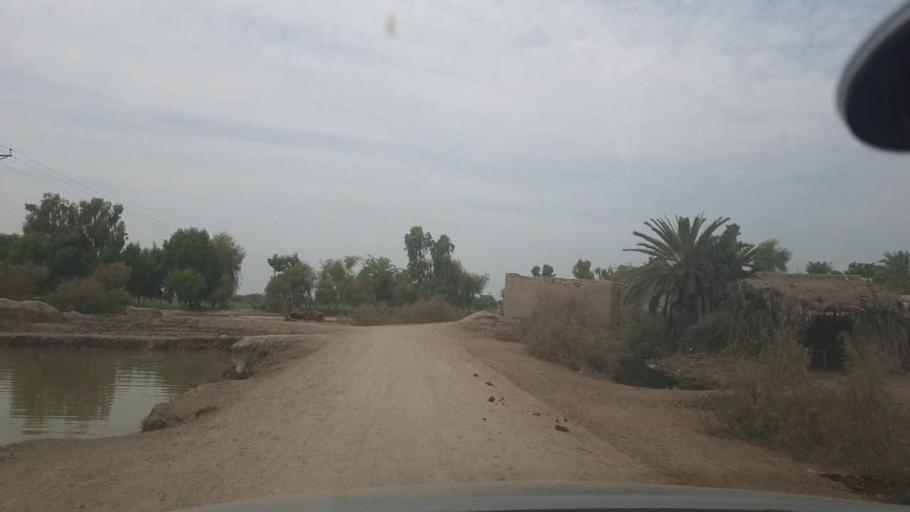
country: PK
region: Balochistan
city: Mehrabpur
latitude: 28.0634
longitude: 68.1389
